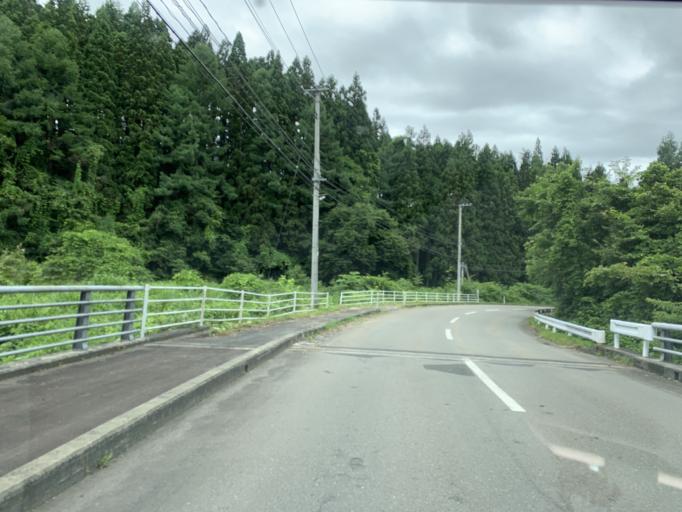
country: JP
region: Iwate
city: Ichinoseki
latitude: 38.9683
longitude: 140.9384
